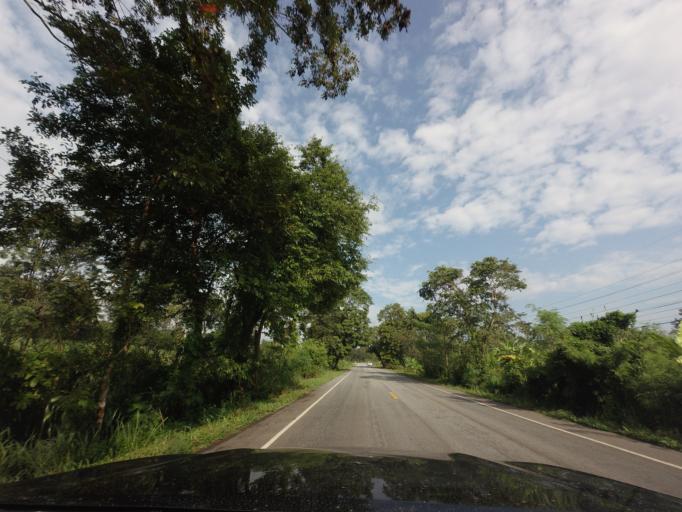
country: TH
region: Nong Khai
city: Pho Tak
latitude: 17.8048
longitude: 102.3420
